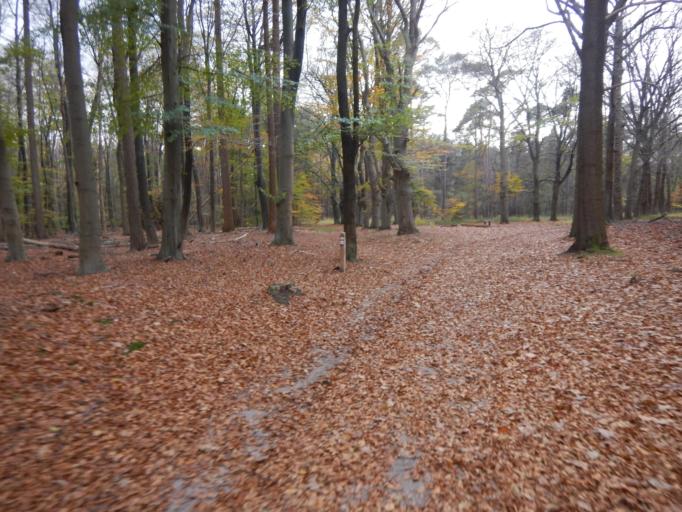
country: NL
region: Gelderland
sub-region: Gemeente Apeldoorn
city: Uddel
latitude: 52.2832
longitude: 5.7529
